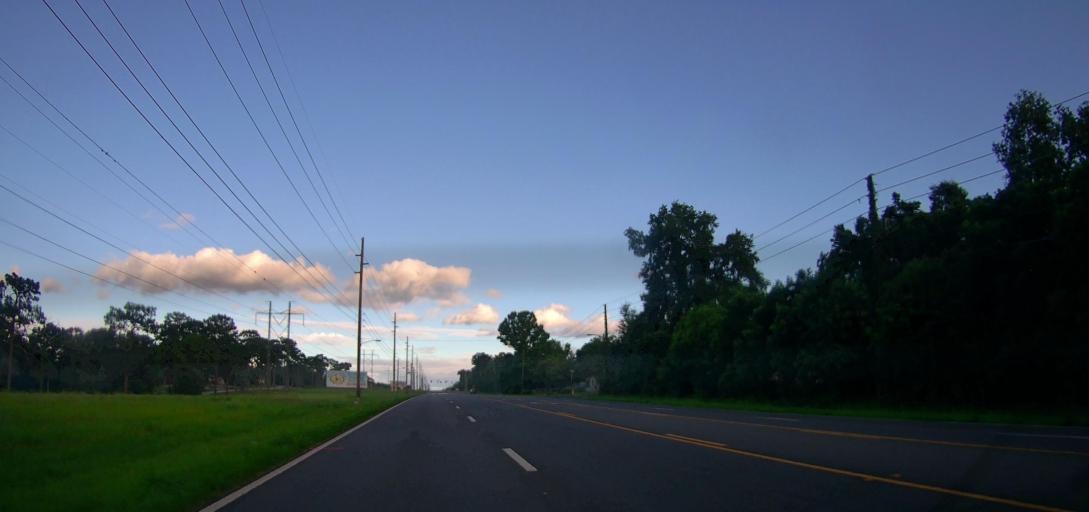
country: US
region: Florida
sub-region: Marion County
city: Silver Springs Shores
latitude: 29.1001
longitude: -82.0083
